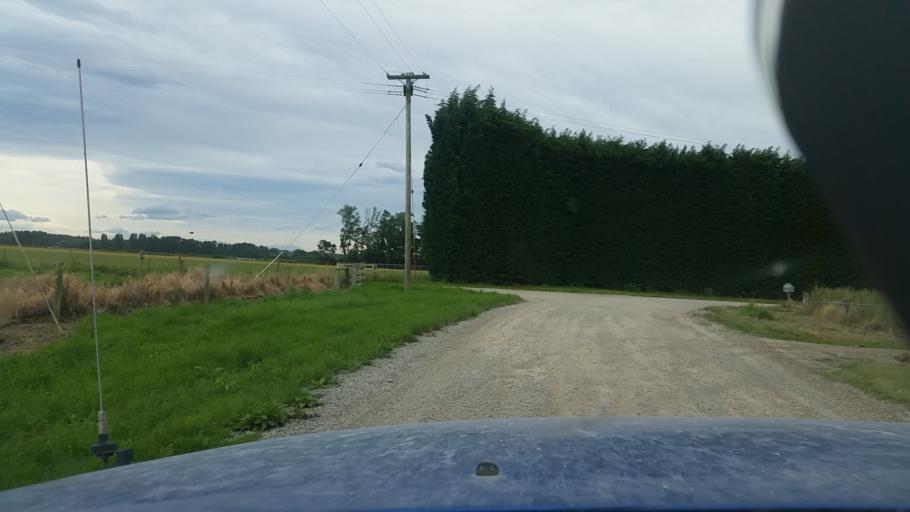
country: NZ
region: Canterbury
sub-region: Ashburton District
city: Ashburton
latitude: -43.8140
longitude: 171.6240
